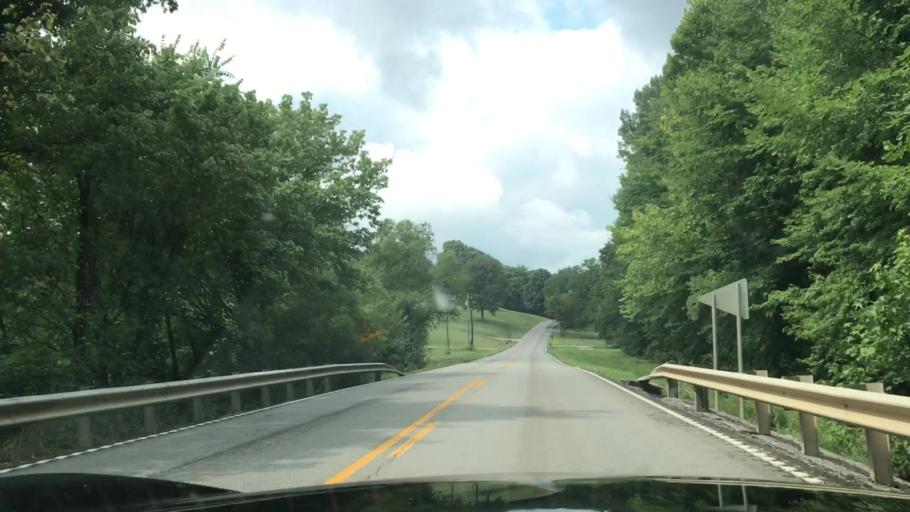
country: US
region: Kentucky
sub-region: Muhlenberg County
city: Central City
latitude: 37.2085
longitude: -87.0708
